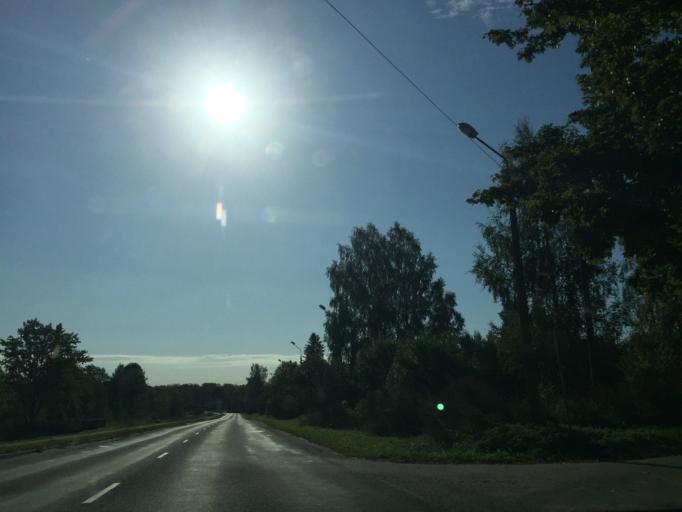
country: LV
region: Limbazu Rajons
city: Limbazi
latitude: 57.5122
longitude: 24.6922
